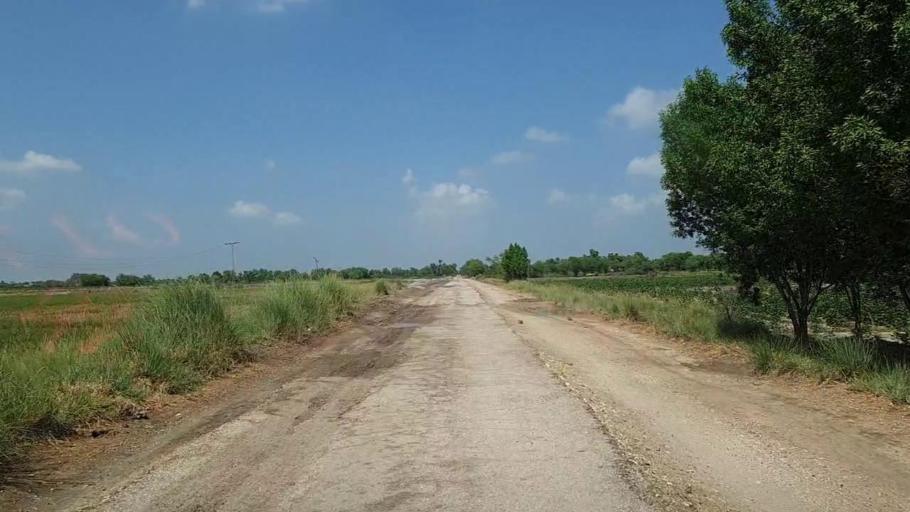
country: PK
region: Sindh
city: Kandiaro
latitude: 27.0175
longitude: 68.2684
